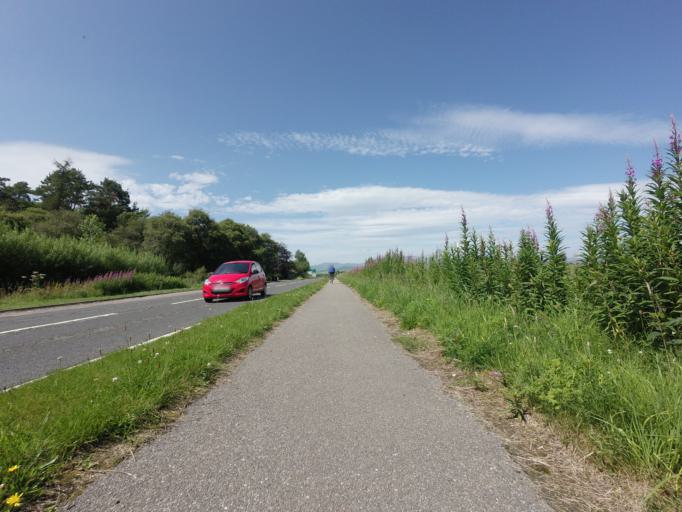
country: GB
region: Scotland
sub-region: Highland
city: Conon Bridge
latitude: 57.5477
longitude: -4.3897
